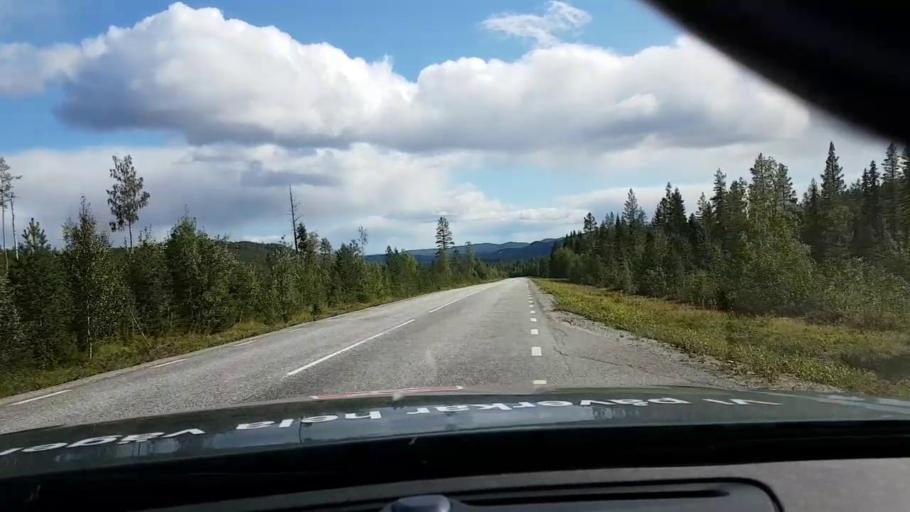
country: SE
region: Vaesterbotten
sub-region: Asele Kommun
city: Asele
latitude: 63.7685
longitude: 17.6827
